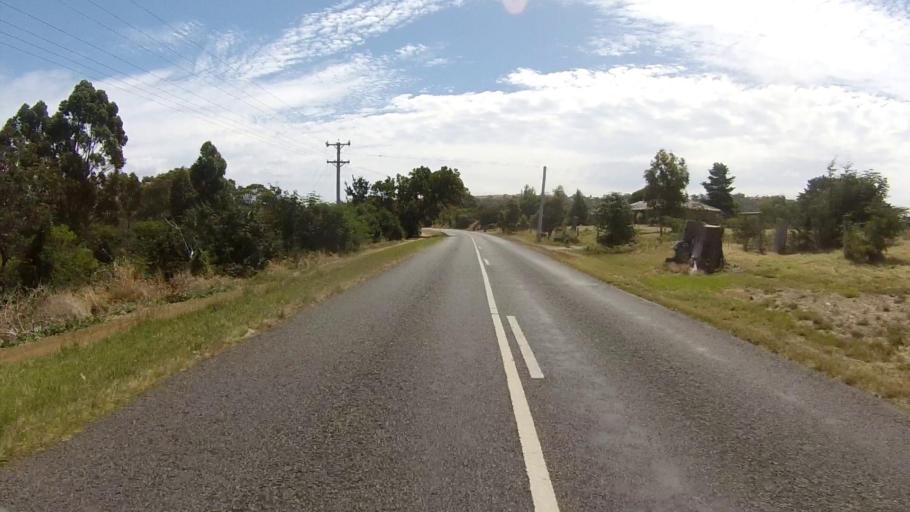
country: AU
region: Tasmania
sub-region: Kingborough
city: Taroona
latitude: -43.0113
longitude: 147.4130
